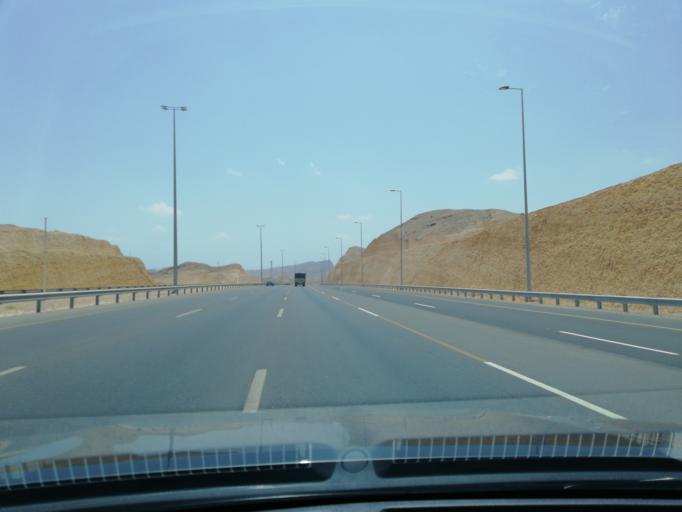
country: OM
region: Muhafazat Masqat
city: As Sib al Jadidah
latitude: 23.5579
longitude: 58.2236
